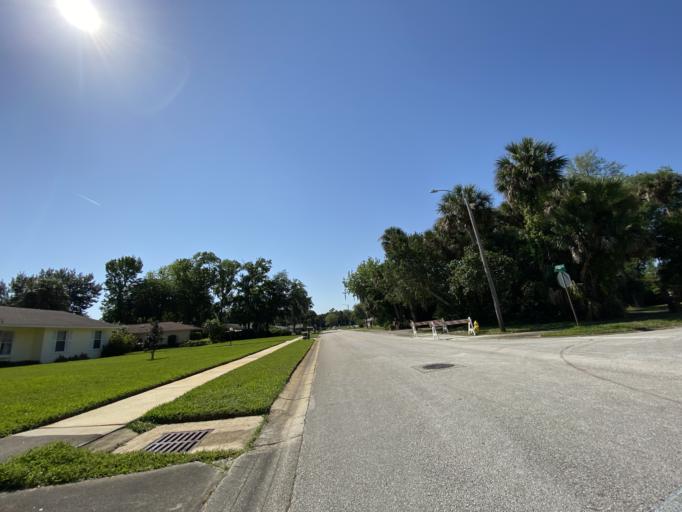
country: US
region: Florida
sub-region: Volusia County
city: South Daytona
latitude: 29.1604
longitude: -81.0105
